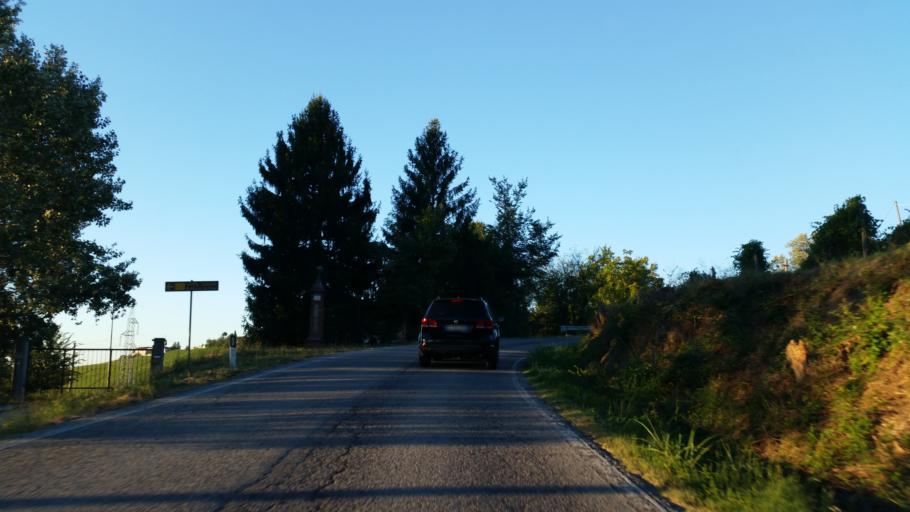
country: IT
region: Piedmont
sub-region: Provincia di Cuneo
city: Bricco di Neive
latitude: 44.7079
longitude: 8.1286
